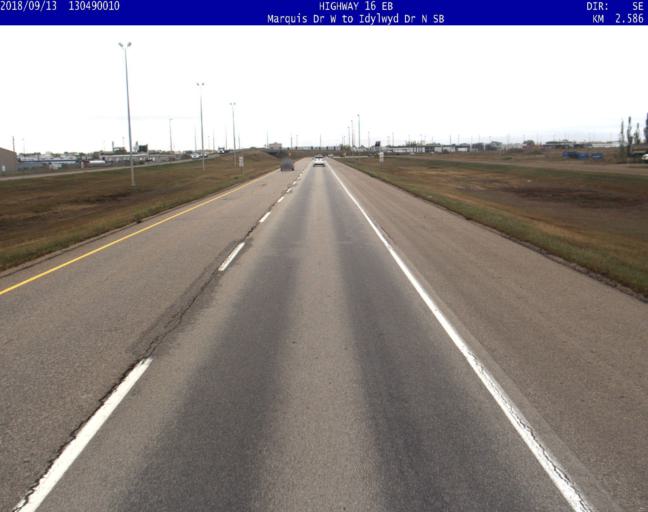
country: CA
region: Saskatchewan
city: Saskatoon
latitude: 52.1859
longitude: -106.6779
